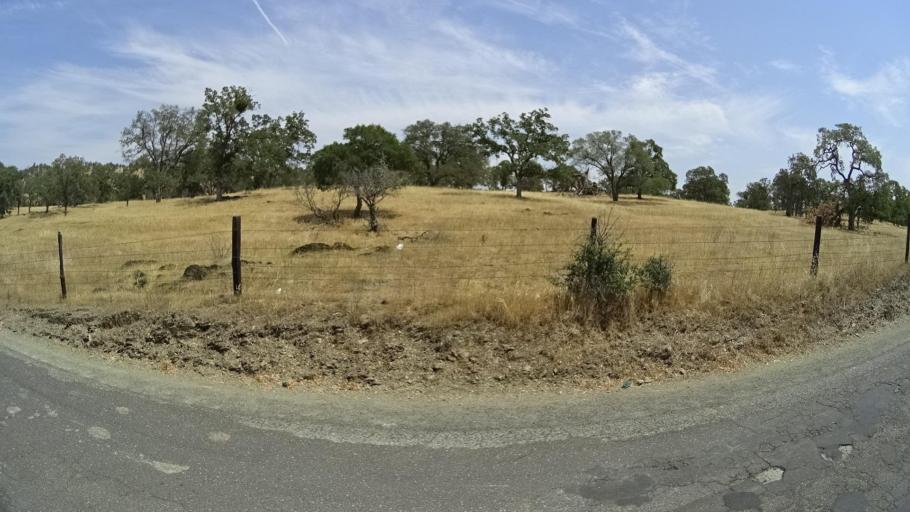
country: US
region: California
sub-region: Tuolumne County
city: Tuolumne City
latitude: 37.6633
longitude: -120.3140
